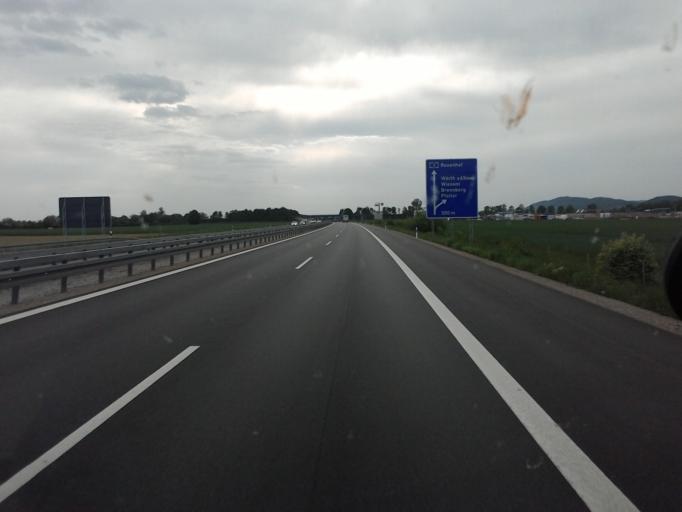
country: DE
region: Bavaria
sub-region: Upper Palatinate
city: Wiesent
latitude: 49.0003
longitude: 12.3726
